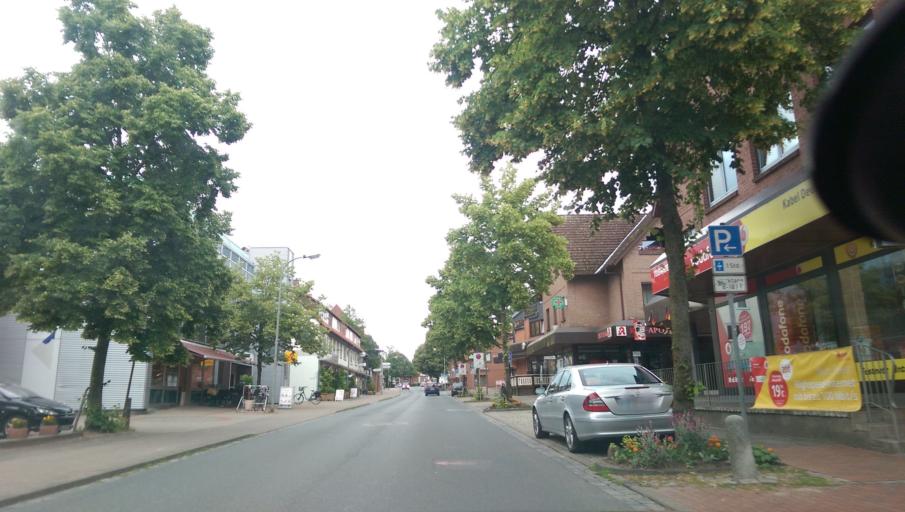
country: DE
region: Lower Saxony
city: Bad Fallingbostel
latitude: 52.8658
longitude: 9.6962
